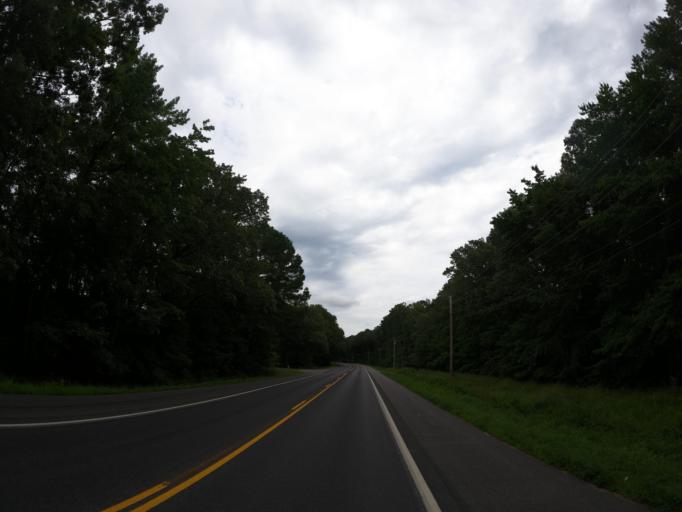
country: US
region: Maryland
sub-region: Saint Mary's County
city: Lexington Park
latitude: 38.1768
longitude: -76.5190
